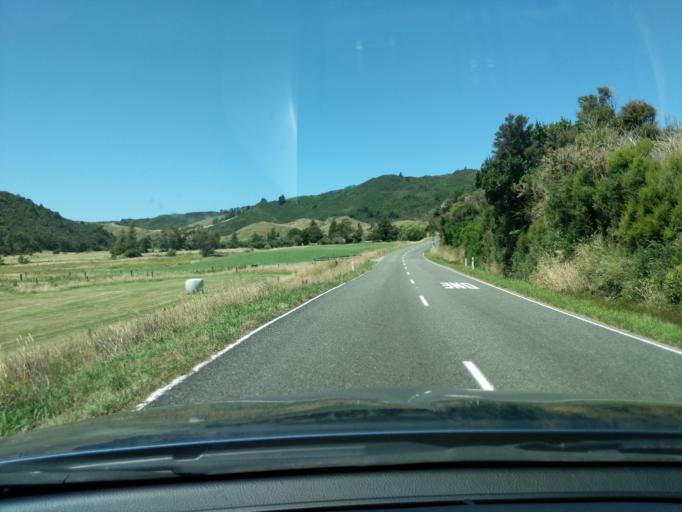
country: NZ
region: Tasman
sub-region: Tasman District
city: Takaka
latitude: -40.7413
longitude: 172.5683
